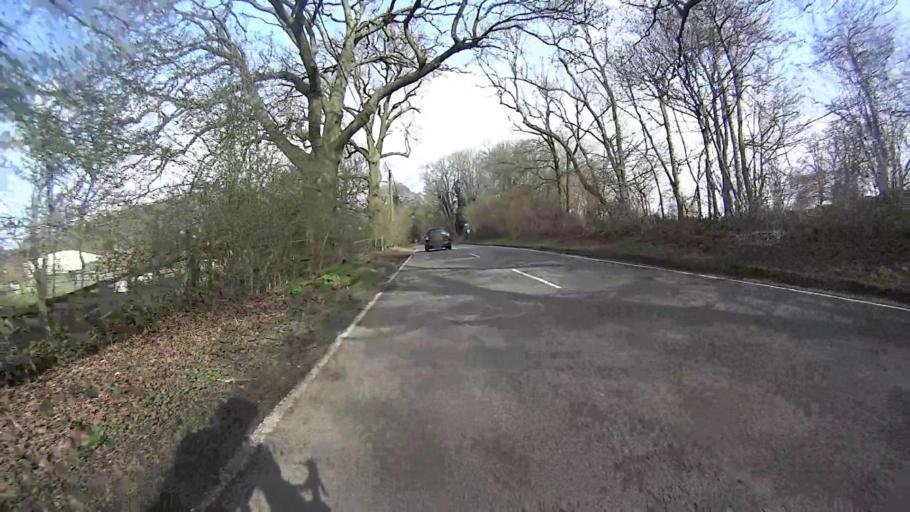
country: GB
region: England
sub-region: Surrey
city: Headley
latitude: 51.2556
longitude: -0.2743
